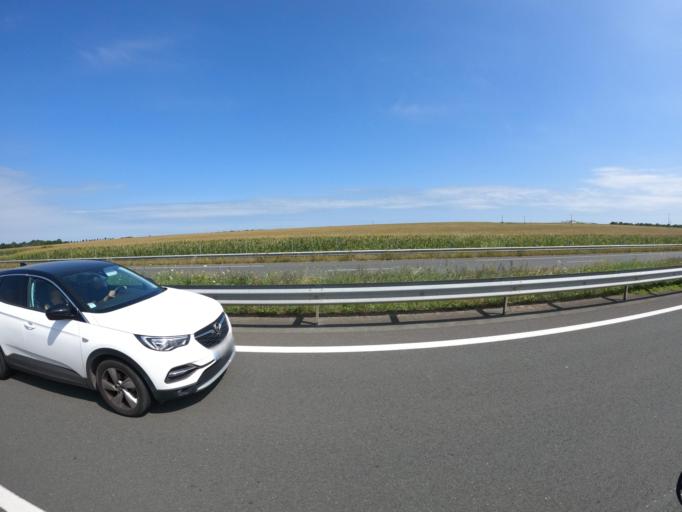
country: FR
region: Poitou-Charentes
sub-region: Departement des Deux-Sevres
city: Mauze-sur-le-Mignon
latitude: 46.2009
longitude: -0.7116
